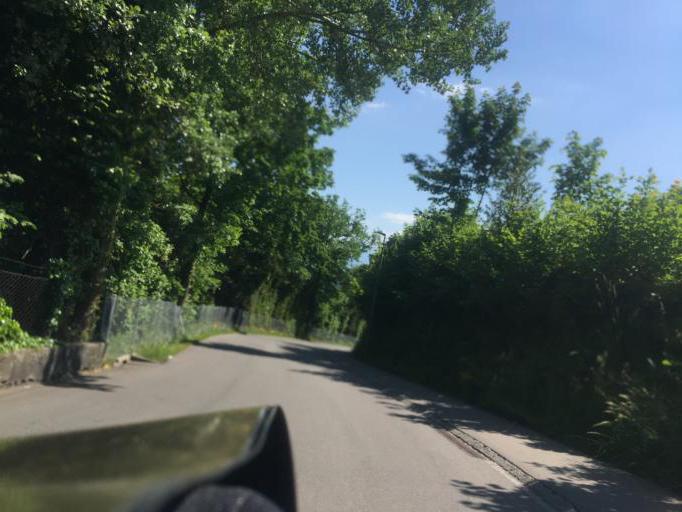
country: CH
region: Bern
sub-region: Bern-Mittelland District
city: Niederwichtrach
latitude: 46.8432
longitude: 7.5443
